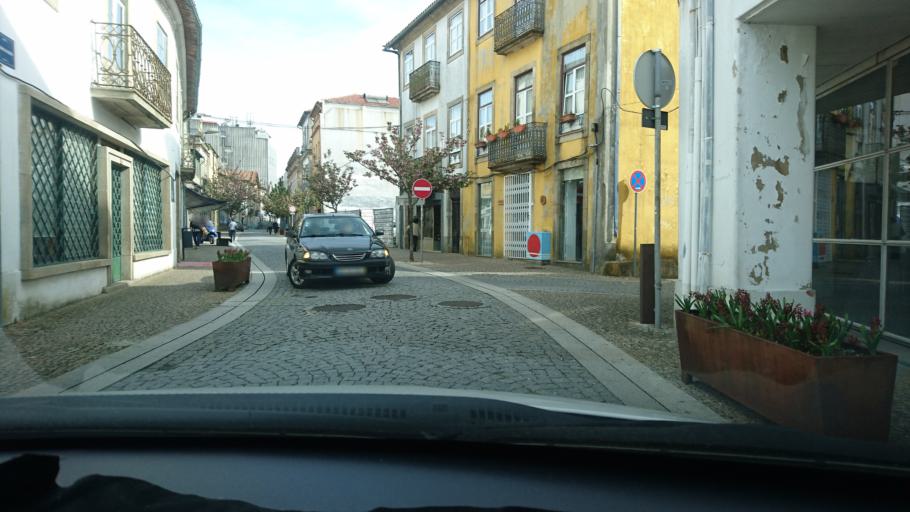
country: PT
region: Aveiro
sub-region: Oliveira de Azemeis
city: Oliveira de Azemeis
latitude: 40.8371
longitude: -8.4781
